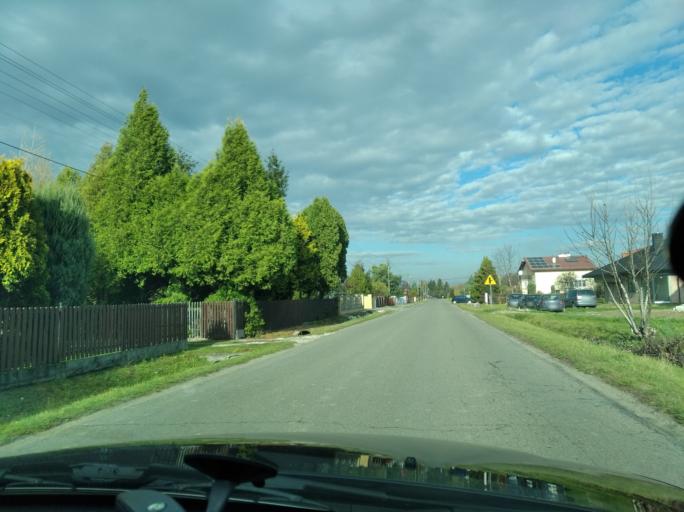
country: PL
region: Subcarpathian Voivodeship
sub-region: Powiat debicki
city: Brzeznica
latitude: 50.0757
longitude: 21.5263
